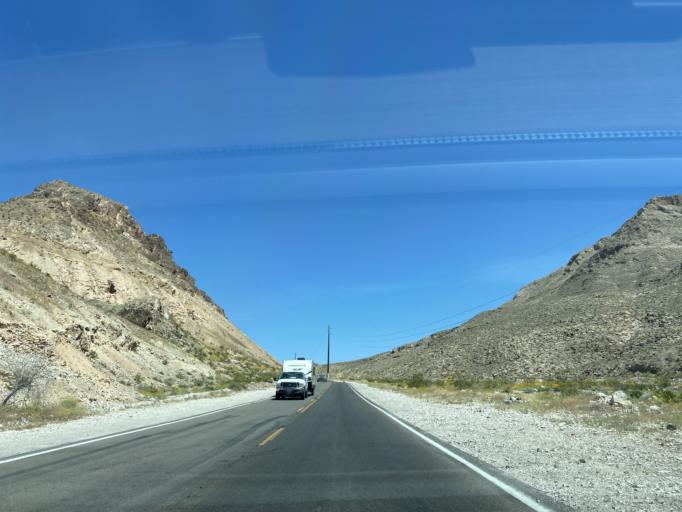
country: US
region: Nevada
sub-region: Clark County
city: Sunrise Manor
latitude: 36.1991
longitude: -115.0037
